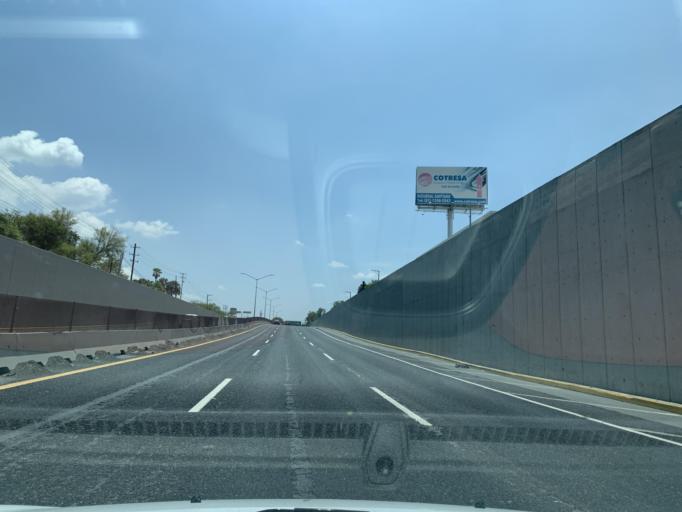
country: MX
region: Nuevo Leon
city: Santiago
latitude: 25.4313
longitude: -100.1518
